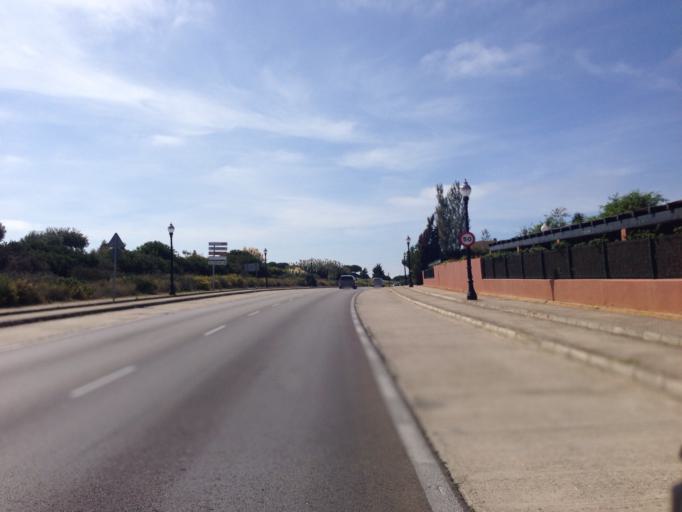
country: ES
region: Andalusia
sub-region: Provincia de Cadiz
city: Chiclana de la Frontera
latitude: 36.3434
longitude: -6.1542
